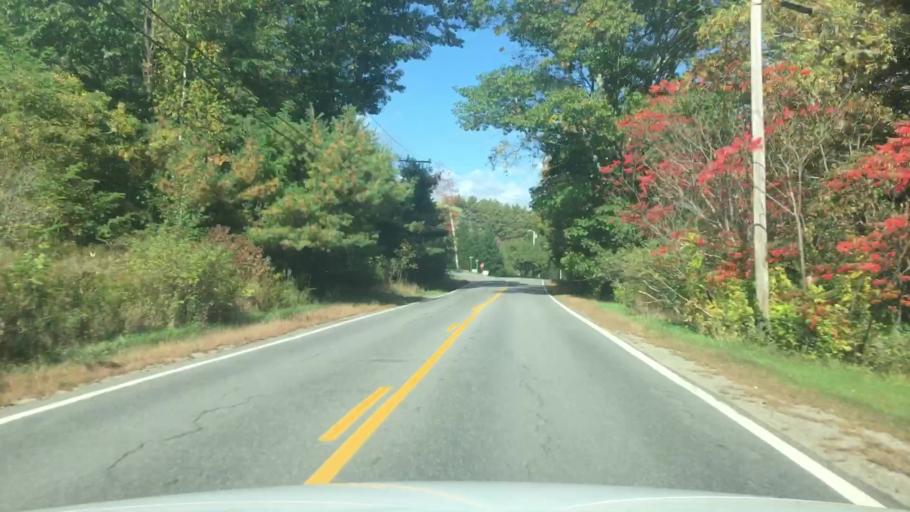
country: US
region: Maine
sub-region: Knox County
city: Union
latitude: 44.2324
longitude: -69.2818
